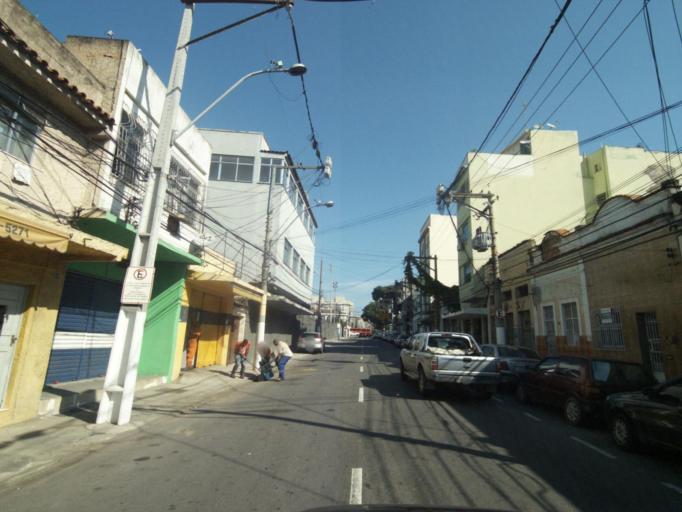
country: BR
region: Rio de Janeiro
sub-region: Niteroi
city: Niteroi
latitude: -22.8834
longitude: -43.1216
